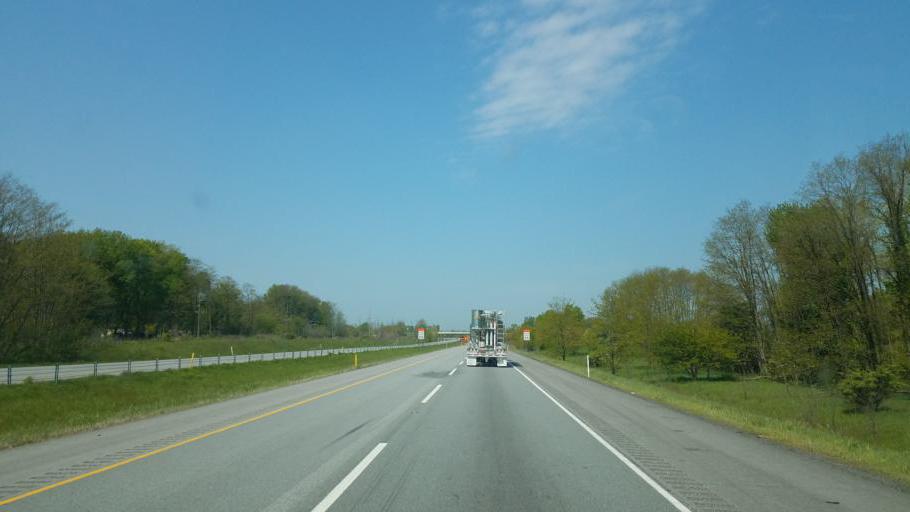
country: US
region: Indiana
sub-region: Porter County
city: South Haven
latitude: 41.5721
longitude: -87.1359
